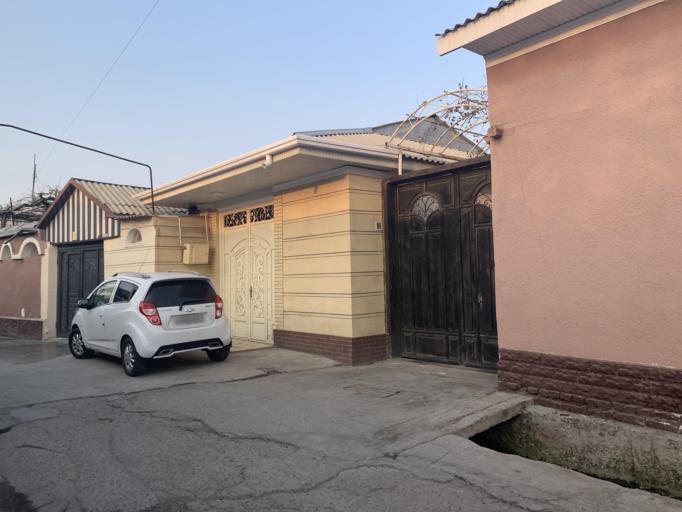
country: UZ
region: Fergana
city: Qo`qon
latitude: 40.5311
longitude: 70.9317
